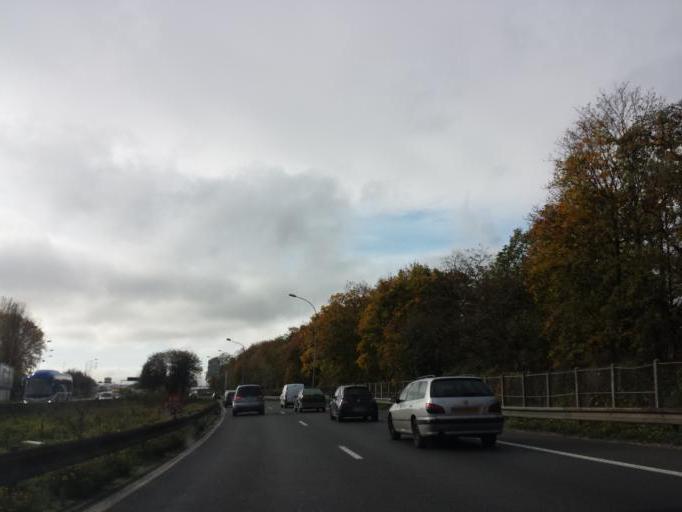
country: FR
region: Ile-de-France
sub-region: Departement du Val-d'Oise
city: Bezons
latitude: 48.9225
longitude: 2.2271
